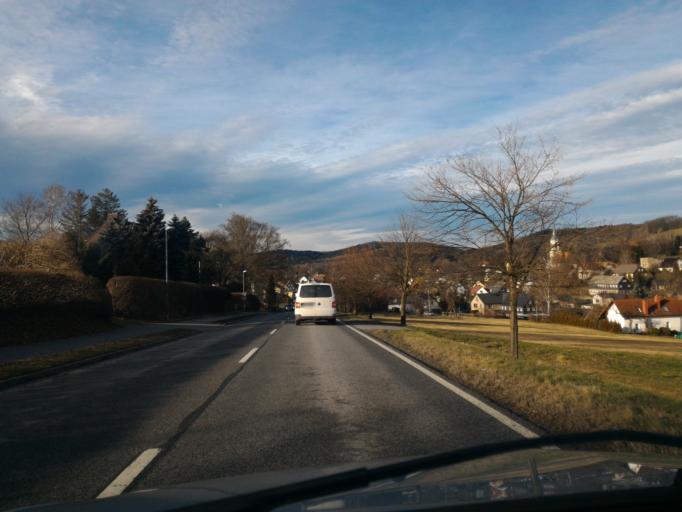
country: DE
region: Saxony
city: Sohland
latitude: 51.0541
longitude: 14.3916
